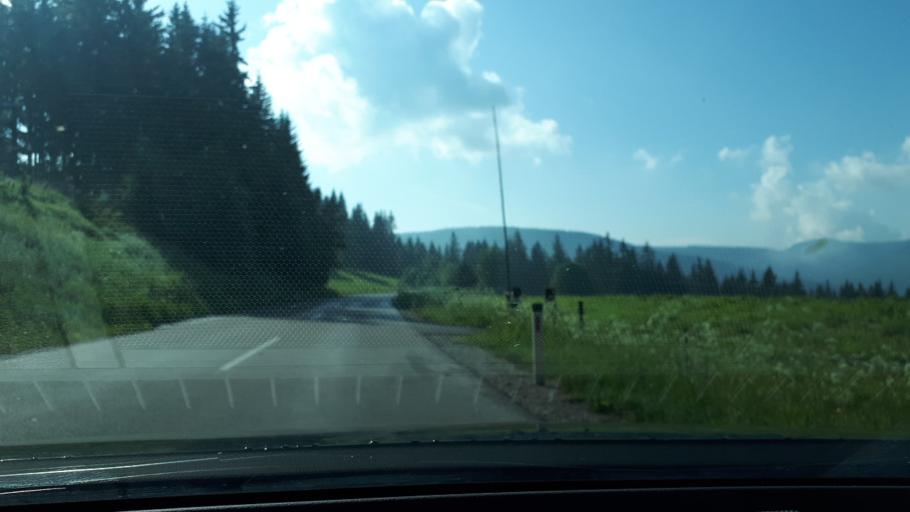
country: AT
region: Styria
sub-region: Politischer Bezirk Voitsberg
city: Pack
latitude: 46.9310
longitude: 14.9925
